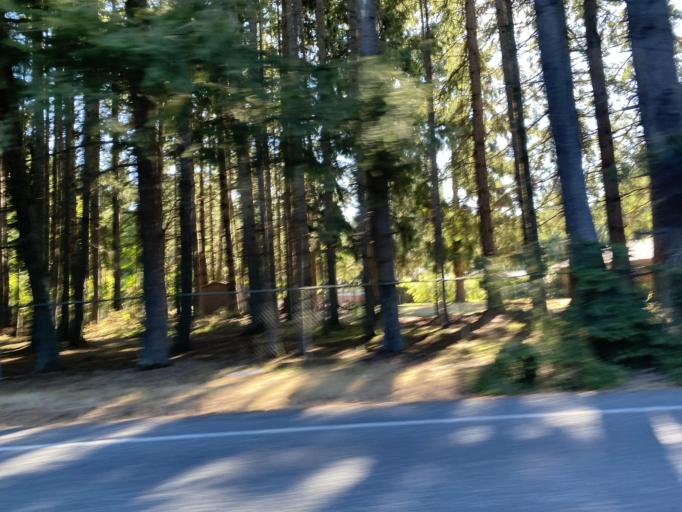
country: US
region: Washington
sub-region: Thurston County
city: Tanglewilde-Thompson Place
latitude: 46.9935
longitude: -122.7387
